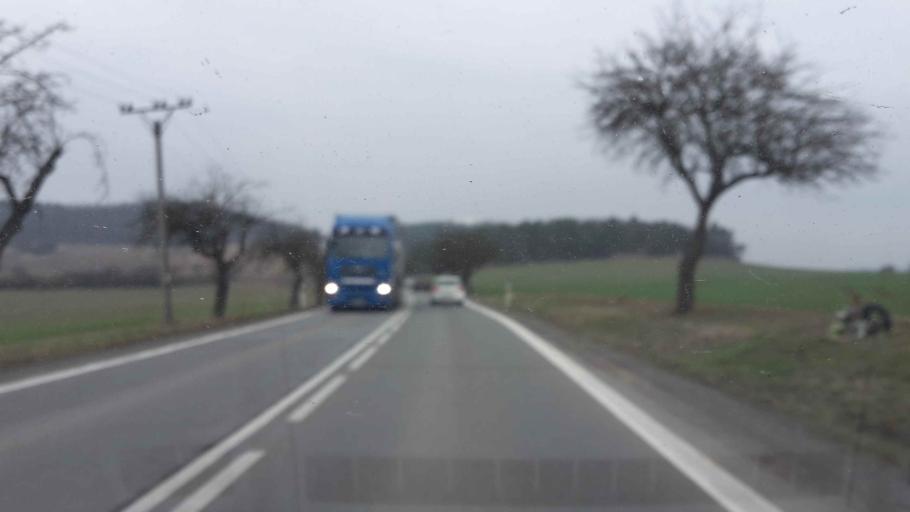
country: CZ
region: South Moravian
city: Kurim
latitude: 49.3053
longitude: 16.5101
